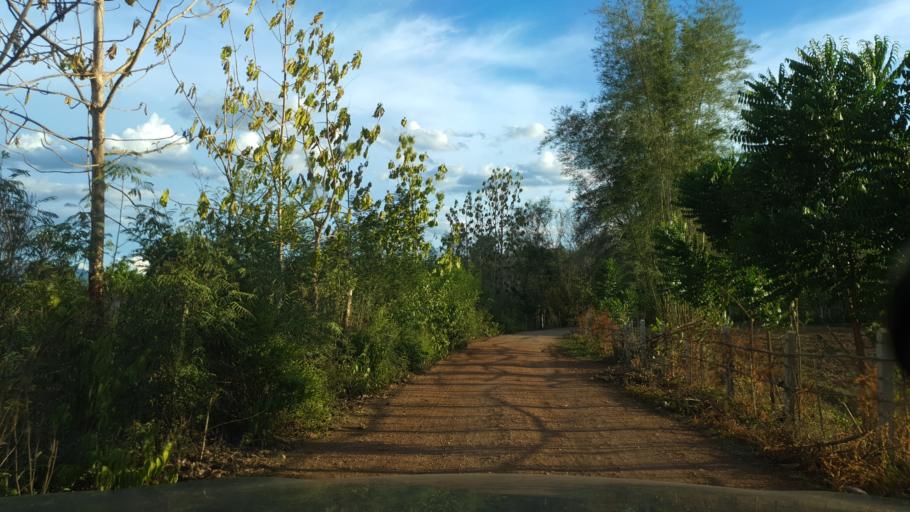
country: TH
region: Lampang
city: Sop Prap
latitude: 17.9571
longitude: 99.3491
